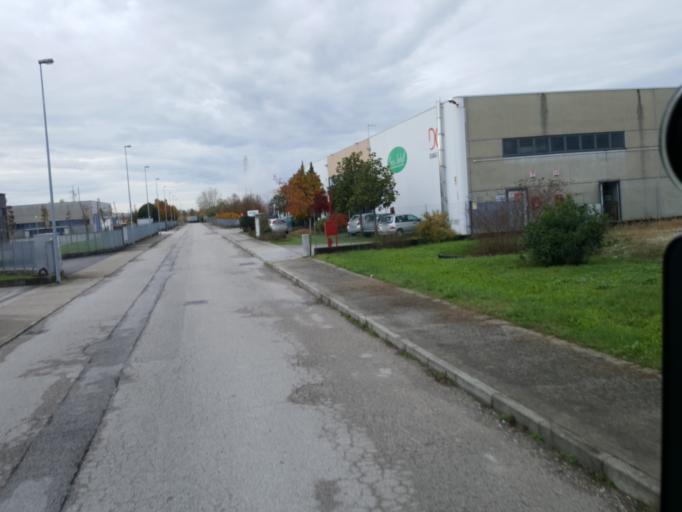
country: IT
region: Friuli Venezia Giulia
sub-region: Provincia di Udine
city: Manzano
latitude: 45.9857
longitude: 13.3581
